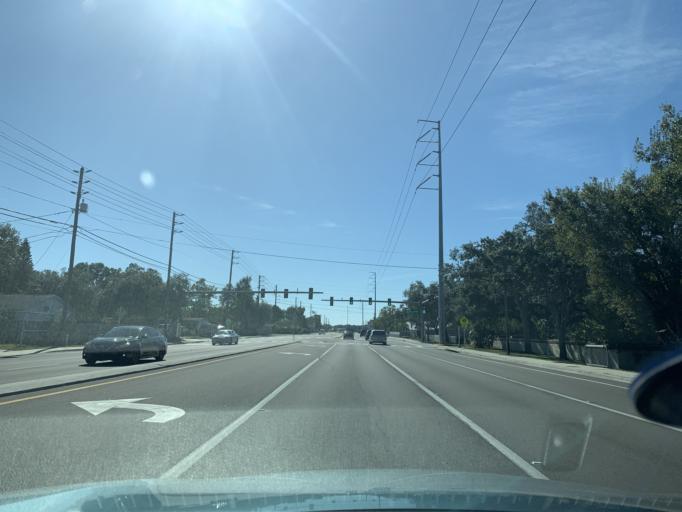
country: US
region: Florida
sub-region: Pinellas County
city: Seminole
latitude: 27.8461
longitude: -82.7624
